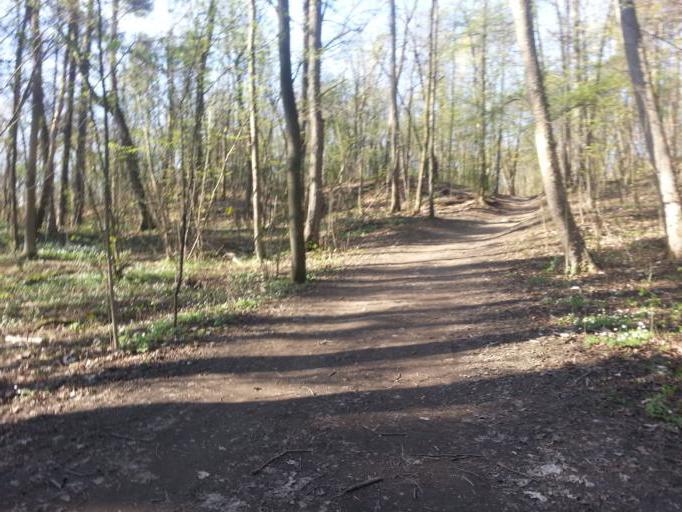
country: NO
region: Oslo
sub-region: Oslo
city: Sjolyststranda
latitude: 59.9163
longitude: 10.6860
